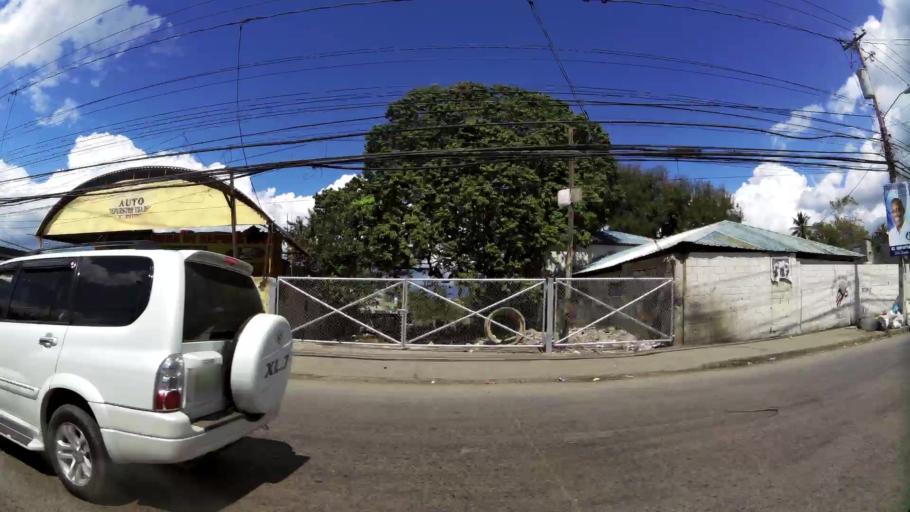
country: DO
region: Santiago
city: Santiago de los Caballeros
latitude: 19.4292
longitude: -70.6886
